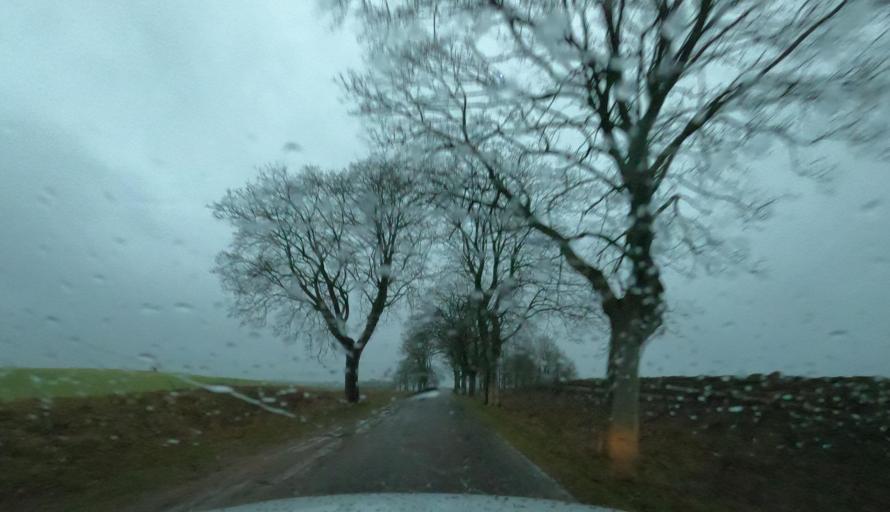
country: PL
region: West Pomeranian Voivodeship
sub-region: Powiat szczecinecki
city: Borne Sulinowo
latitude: 53.7025
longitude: 16.5182
